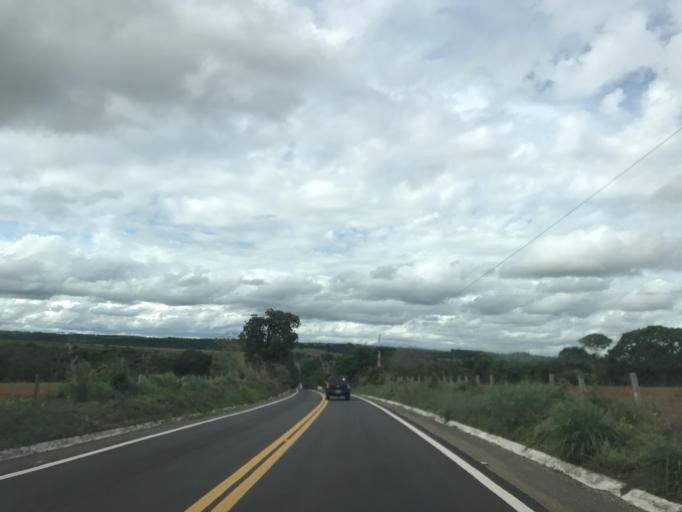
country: BR
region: Goias
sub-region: Bela Vista De Goias
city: Bela Vista de Goias
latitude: -17.1728
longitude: -48.6823
